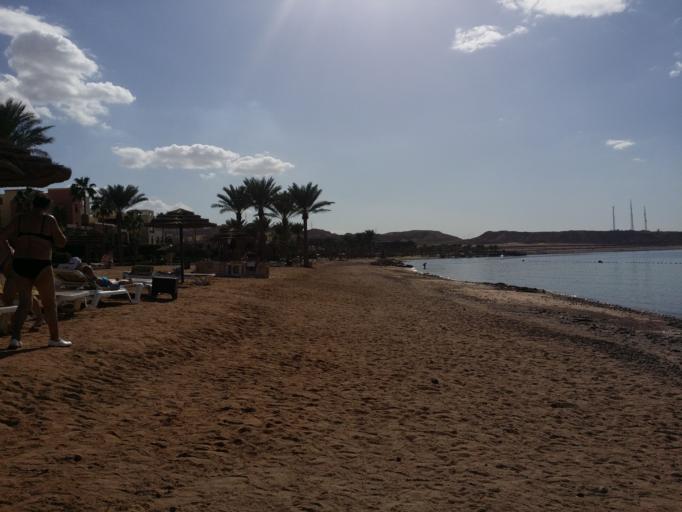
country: JO
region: Aqaba
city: Aqaba
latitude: 29.4107
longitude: 34.9778
